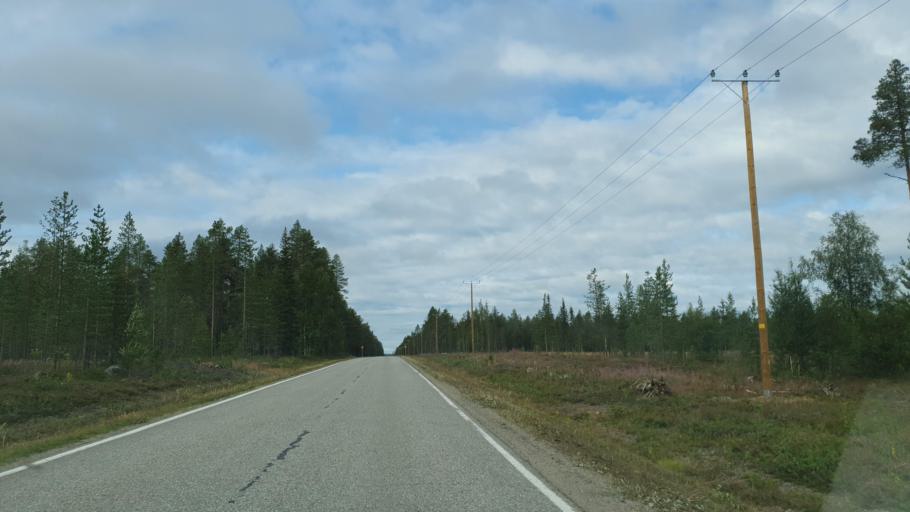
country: FI
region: Lapland
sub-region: Pohjois-Lappi
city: Sodankylae
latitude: 67.4713
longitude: 26.1625
